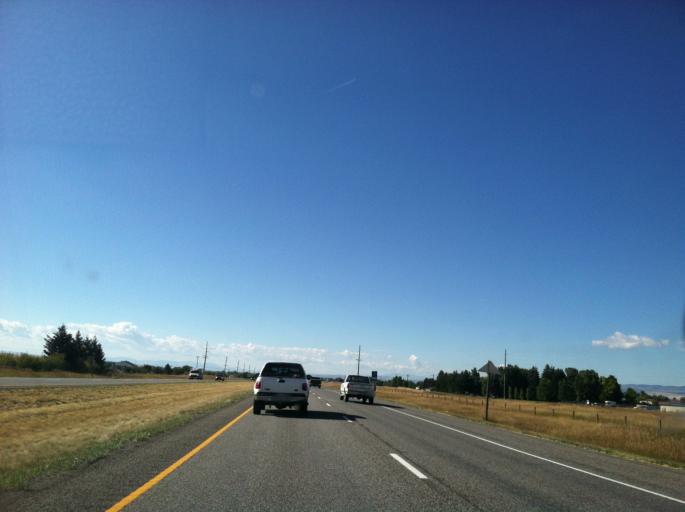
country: US
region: Montana
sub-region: Gallatin County
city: Bozeman
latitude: 45.7350
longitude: -111.1003
